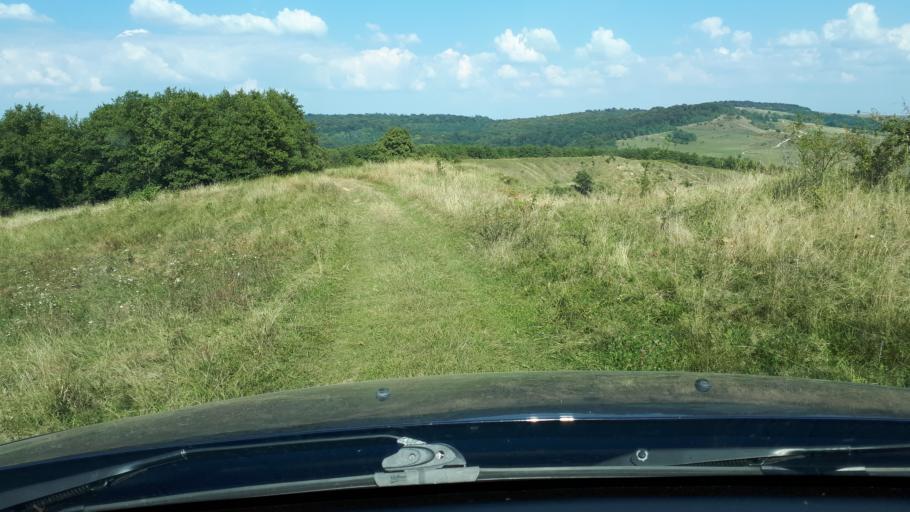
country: RO
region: Brasov
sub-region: Comuna Vistea de Jos
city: Vistea de Jos
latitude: 45.8222
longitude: 24.7487
